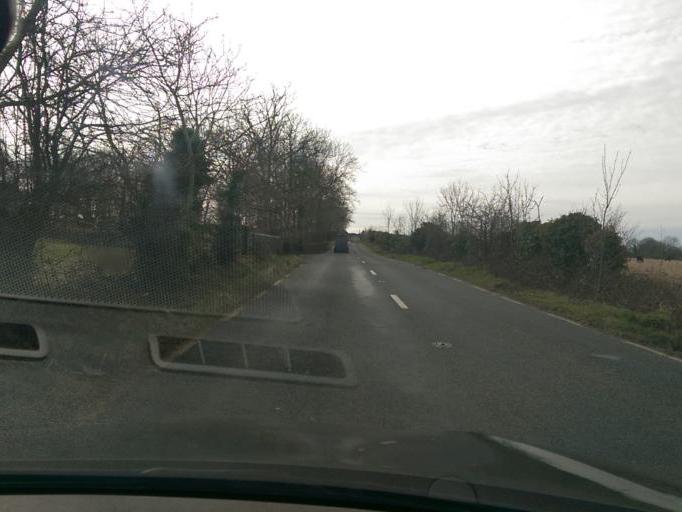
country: IE
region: Connaught
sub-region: County Galway
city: Tuam
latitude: 53.4169
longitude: -8.7968
